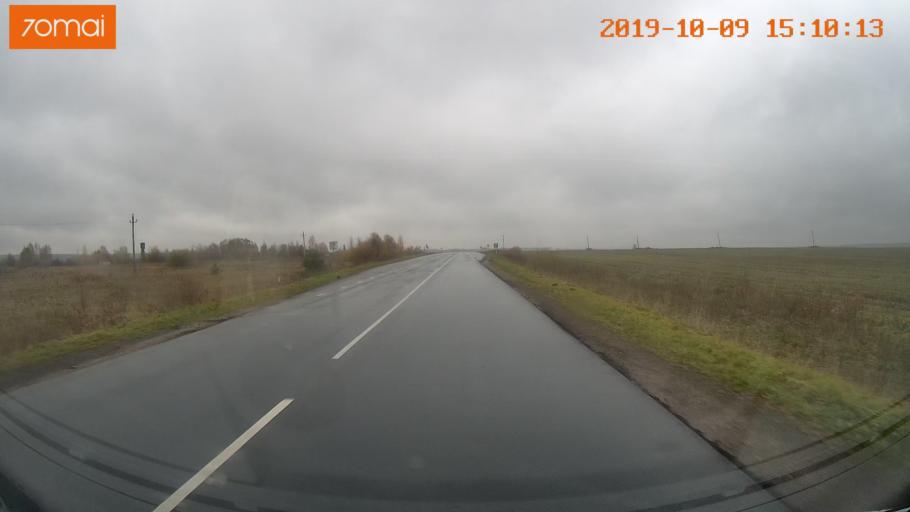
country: RU
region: Kostroma
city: Susanino
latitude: 58.1808
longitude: 41.6432
